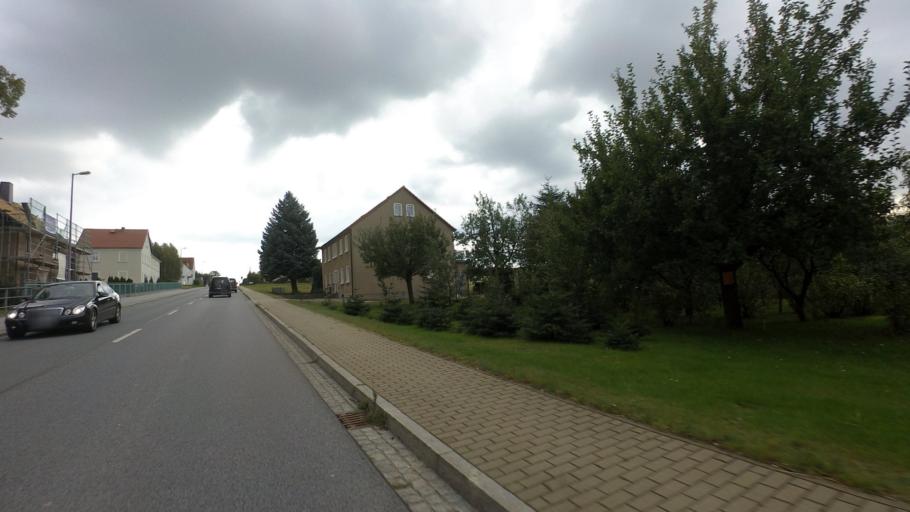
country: DE
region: Saxony
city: Grosspostwitz
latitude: 51.1383
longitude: 14.4417
